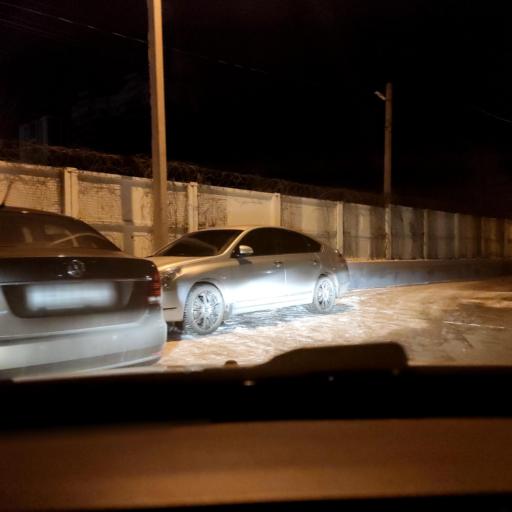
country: RU
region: Voronezj
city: Podgornoye
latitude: 51.7196
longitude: 39.1411
